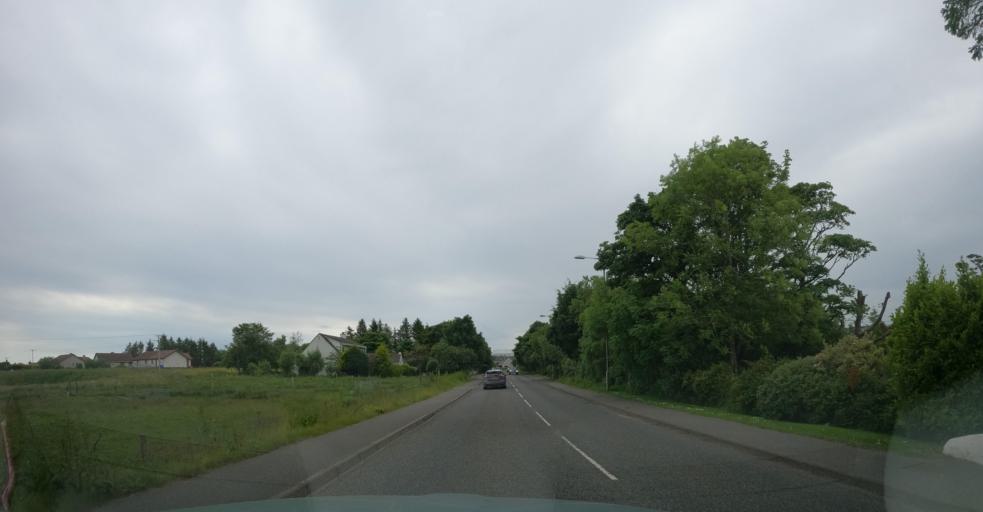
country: GB
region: Scotland
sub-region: Eilean Siar
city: Isle of Lewis
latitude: 58.2259
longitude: -6.3865
